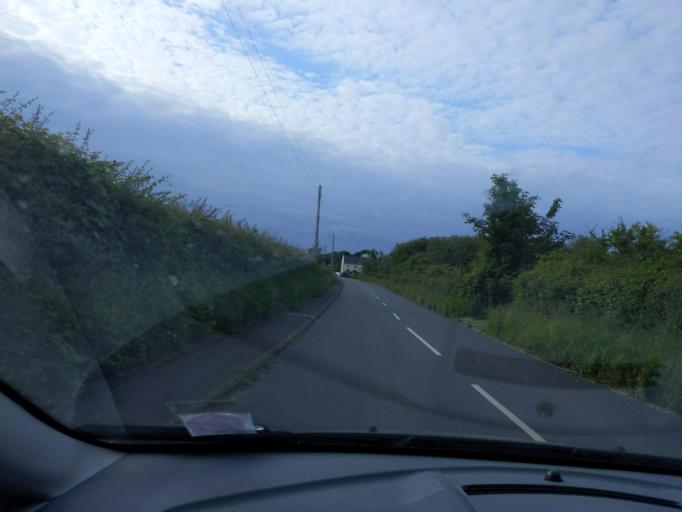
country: IM
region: Ramsey
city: Ramsey
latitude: 54.3651
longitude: -4.4378
